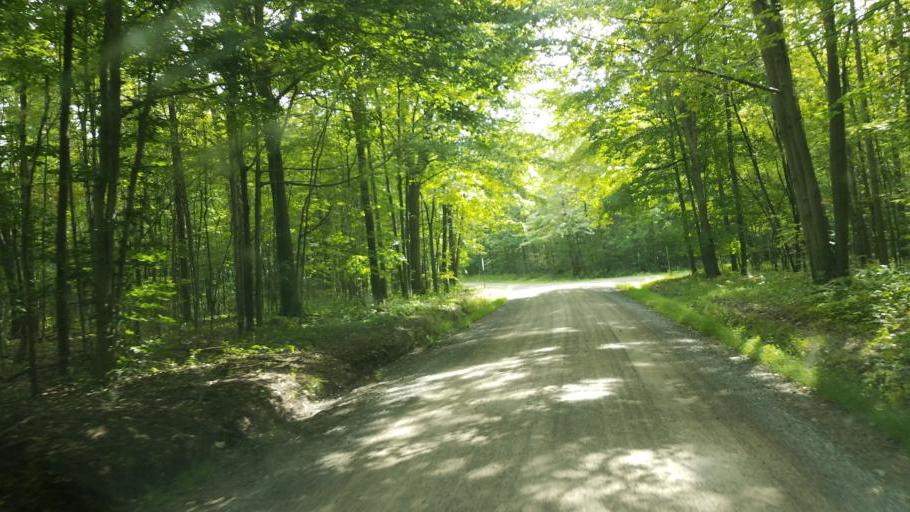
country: US
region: Pennsylvania
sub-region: Crawford County
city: Pymatuning Central
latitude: 41.5415
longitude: -80.4166
